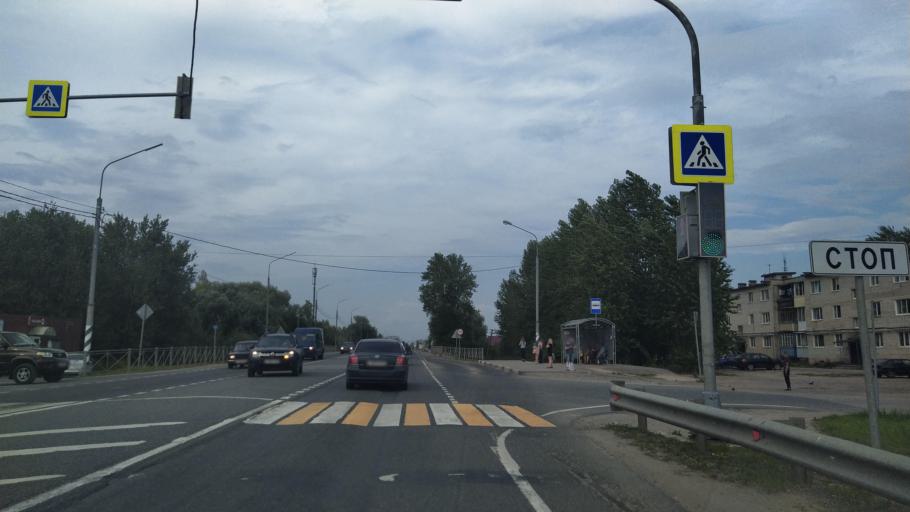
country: RU
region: Novgorod
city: Pankovka
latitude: 58.4900
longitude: 31.2012
